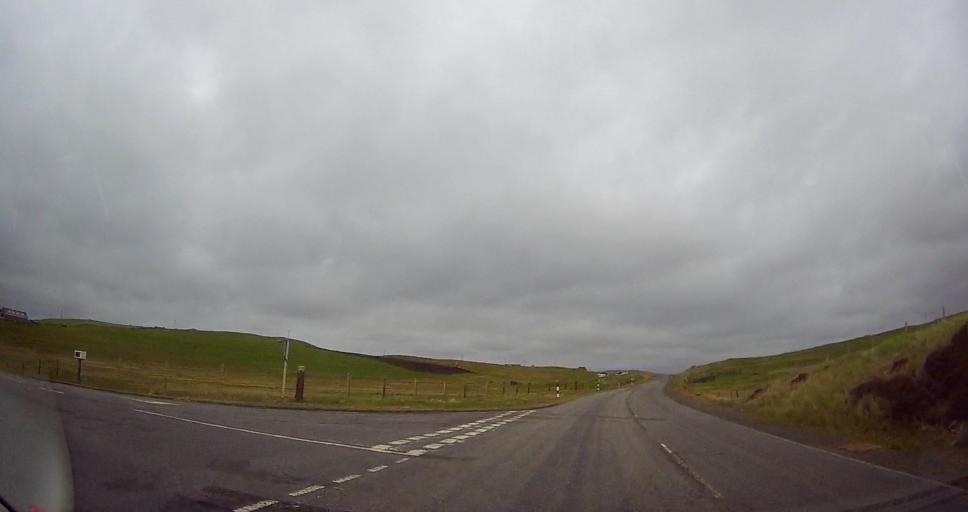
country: GB
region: Scotland
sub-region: Shetland Islands
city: Lerwick
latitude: 60.3730
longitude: -1.3361
